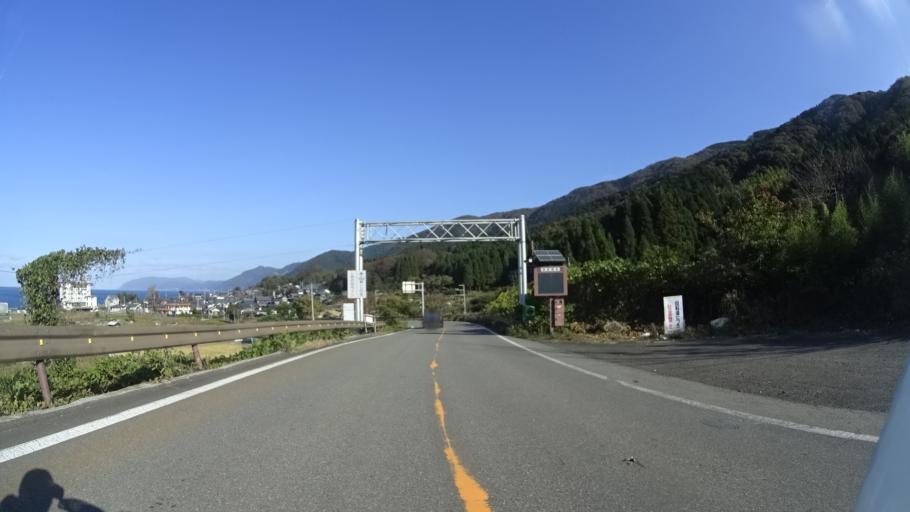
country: JP
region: Fukui
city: Tsuruga
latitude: 35.7441
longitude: 136.1028
